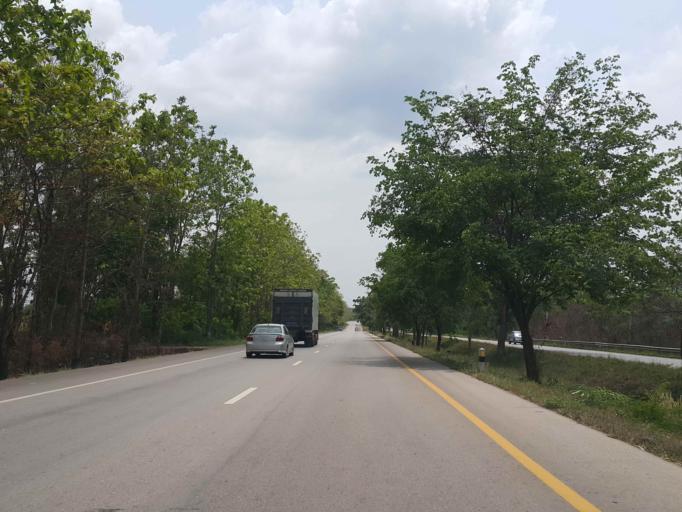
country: TH
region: Lampang
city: Ko Kha
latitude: 18.0642
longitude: 99.3905
